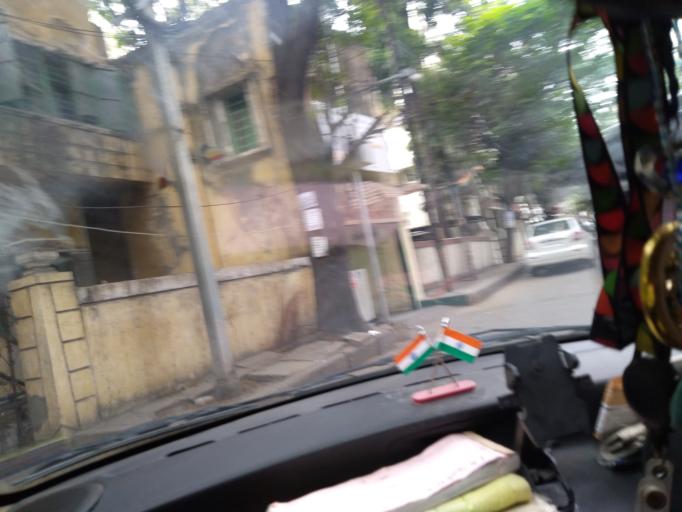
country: IN
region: Telangana
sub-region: Rangareddi
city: Gaddi Annaram
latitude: 17.3902
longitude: 78.4983
